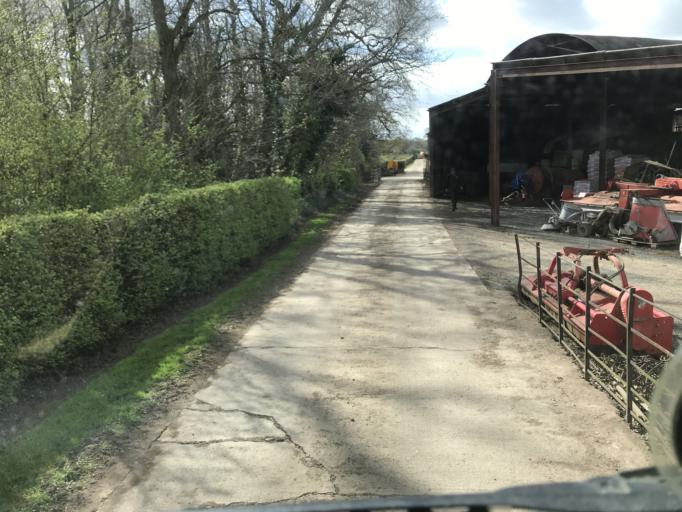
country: GB
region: England
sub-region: Cheshire West and Chester
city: Eccleston
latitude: 53.1534
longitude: -2.8879
